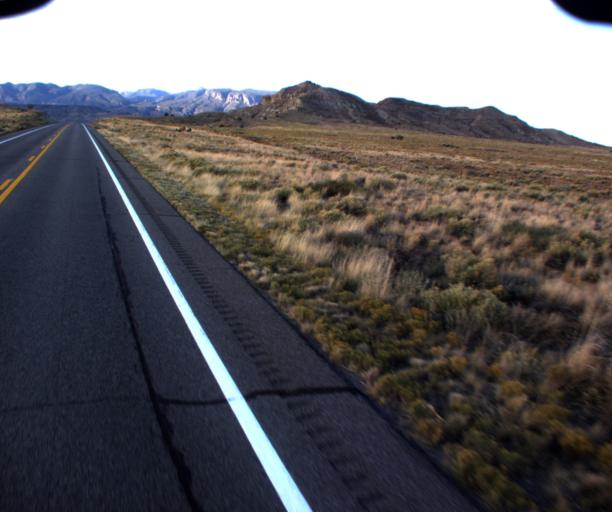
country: US
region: New Mexico
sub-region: San Juan County
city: Shiprock
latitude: 36.9499
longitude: -109.0714
